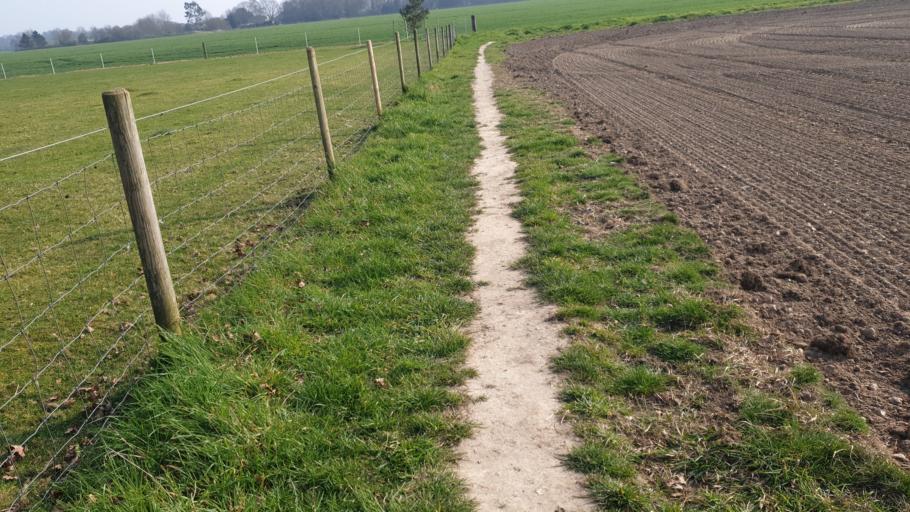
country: GB
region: England
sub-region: Essex
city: Little Clacton
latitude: 51.8795
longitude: 1.1188
